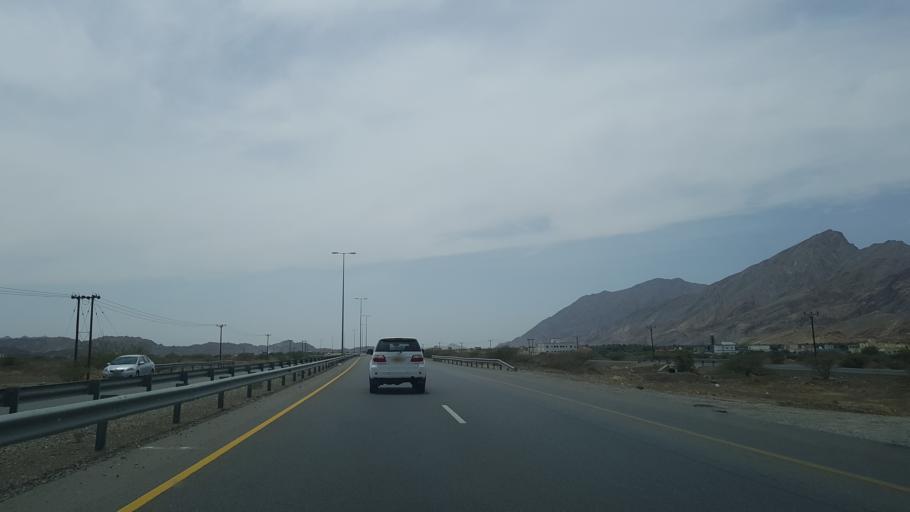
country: OM
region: Muhafazat ad Dakhiliyah
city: Izki
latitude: 23.0176
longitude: 57.7933
